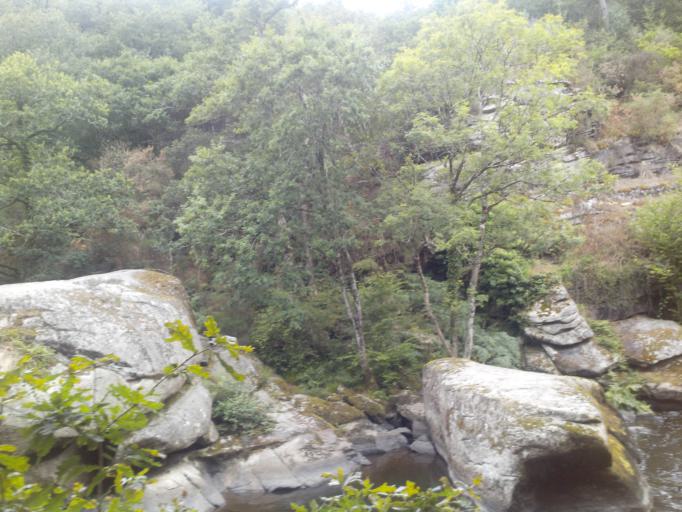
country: FR
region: Brittany
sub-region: Departement du Finistere
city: Arzano
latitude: 47.9447
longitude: -3.4696
